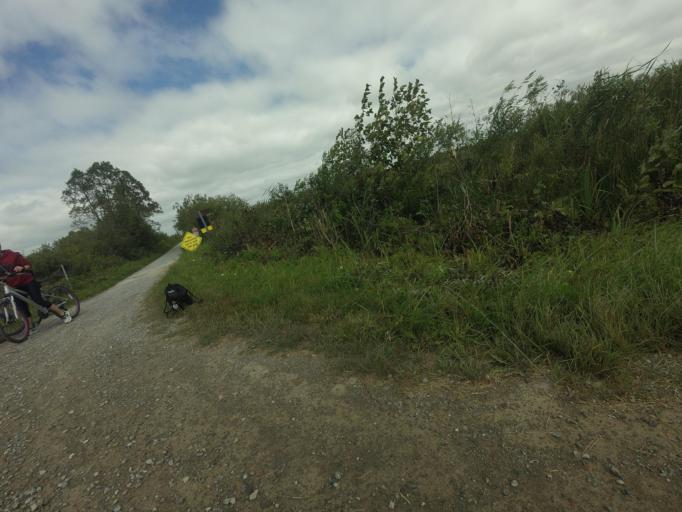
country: CA
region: Ontario
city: Uxbridge
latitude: 44.1766
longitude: -79.0729
